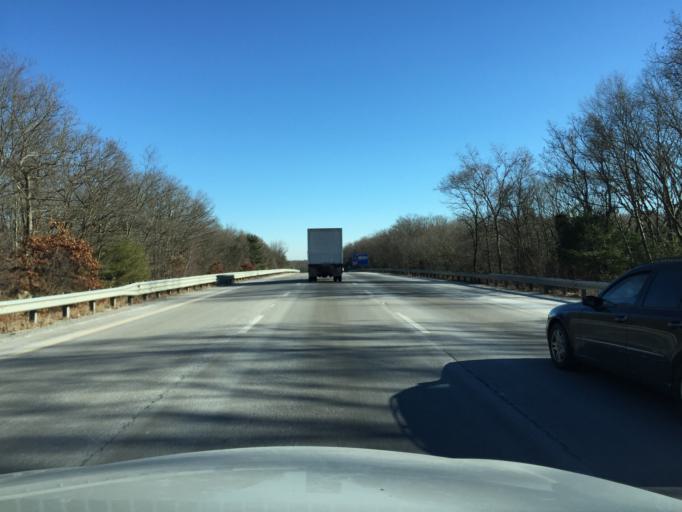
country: US
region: Massachusetts
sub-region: Norfolk County
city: Wrentham
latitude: 42.0385
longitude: -71.3337
